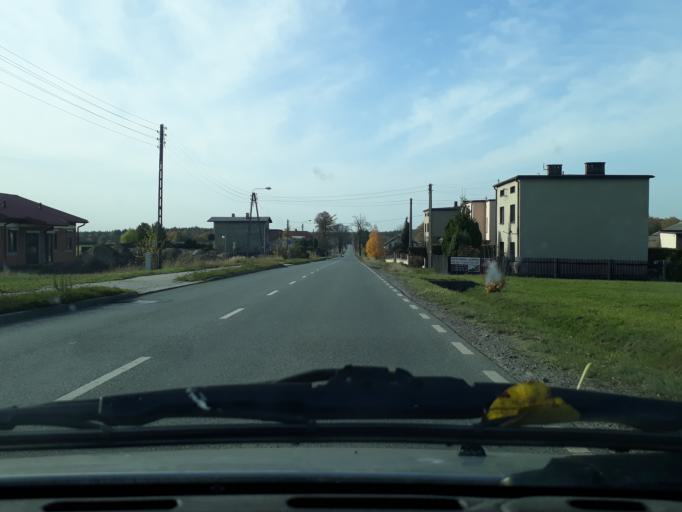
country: PL
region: Silesian Voivodeship
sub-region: Powiat lubliniecki
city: Psary
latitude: 50.5767
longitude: 18.9891
